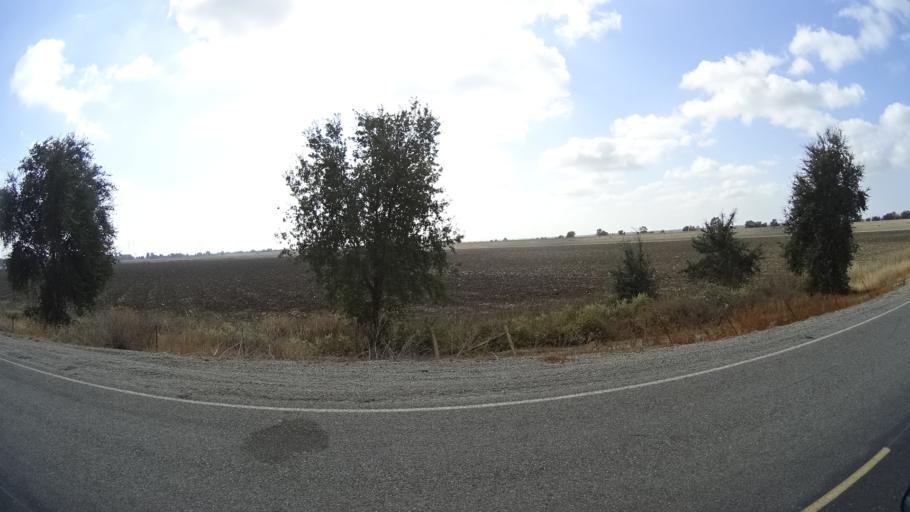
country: US
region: California
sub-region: Yolo County
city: Woodland
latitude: 38.7486
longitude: -121.6889
